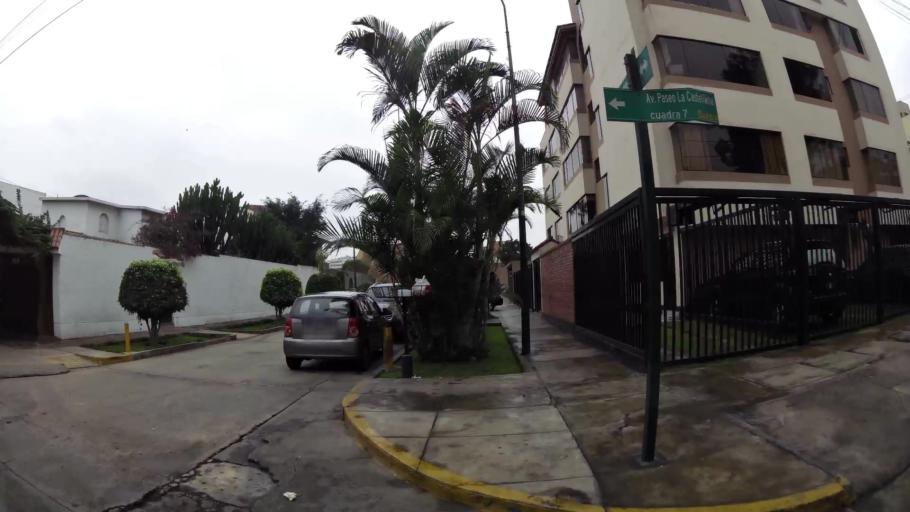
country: PE
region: Lima
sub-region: Lima
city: Surco
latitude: -12.1375
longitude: -77.0056
